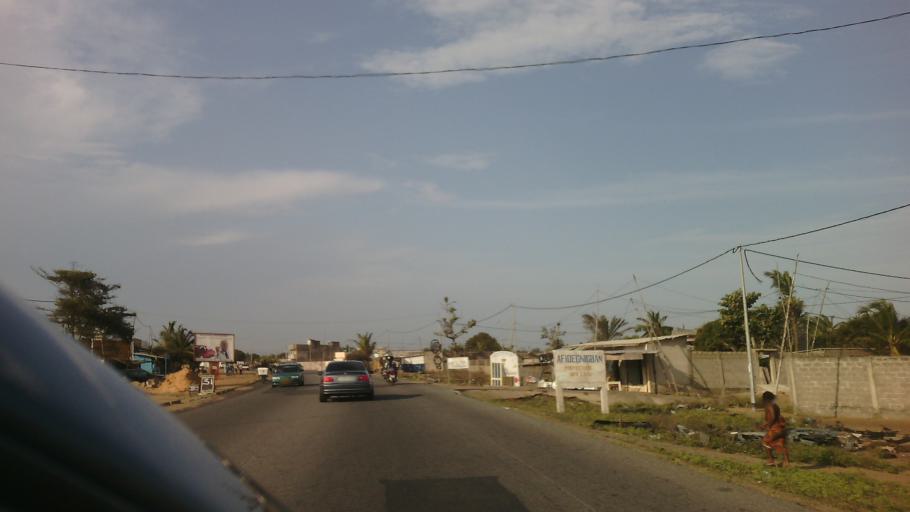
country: TG
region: Maritime
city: Lome
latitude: 6.1824
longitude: 1.3921
